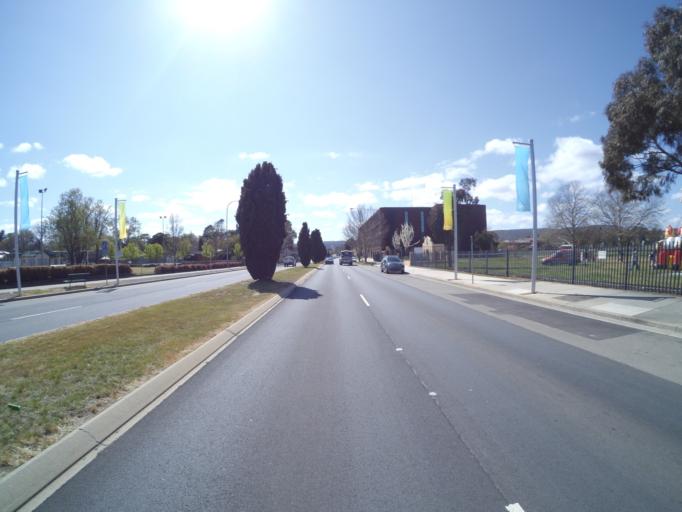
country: AU
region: New South Wales
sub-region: Queanbeyan
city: Queanbeyan
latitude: -35.3557
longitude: 149.2297
